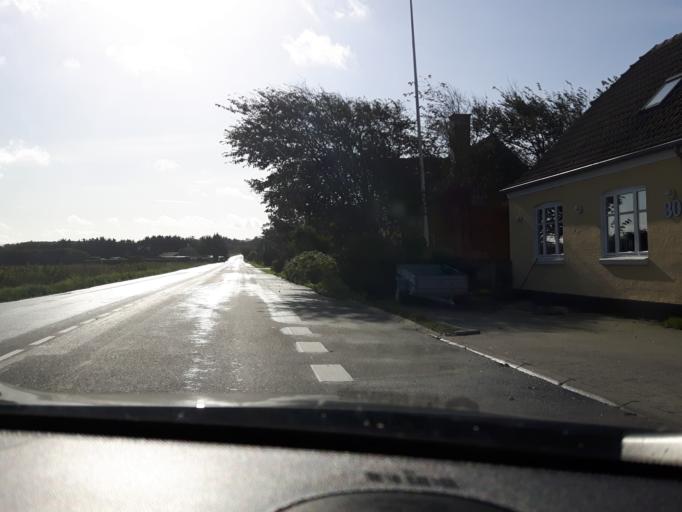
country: DK
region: North Denmark
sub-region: Hjorring Kommune
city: Hjorring
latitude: 57.4663
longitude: 9.8086
